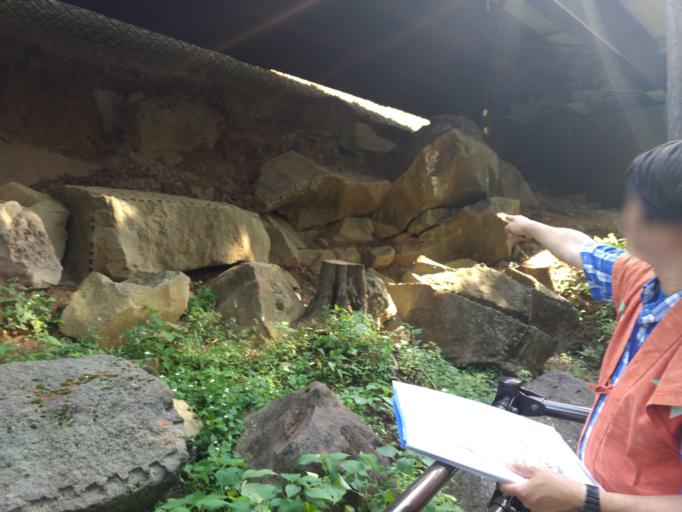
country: JP
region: Kanagawa
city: Odawara
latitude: 35.2318
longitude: 139.1222
